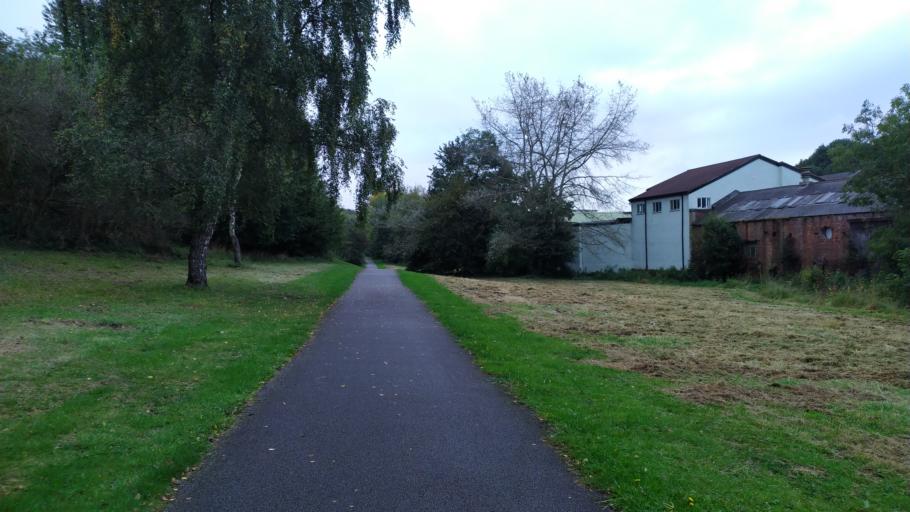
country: GB
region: England
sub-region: City and Borough of Leeds
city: Chapel Allerton
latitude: 53.8186
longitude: -1.5491
